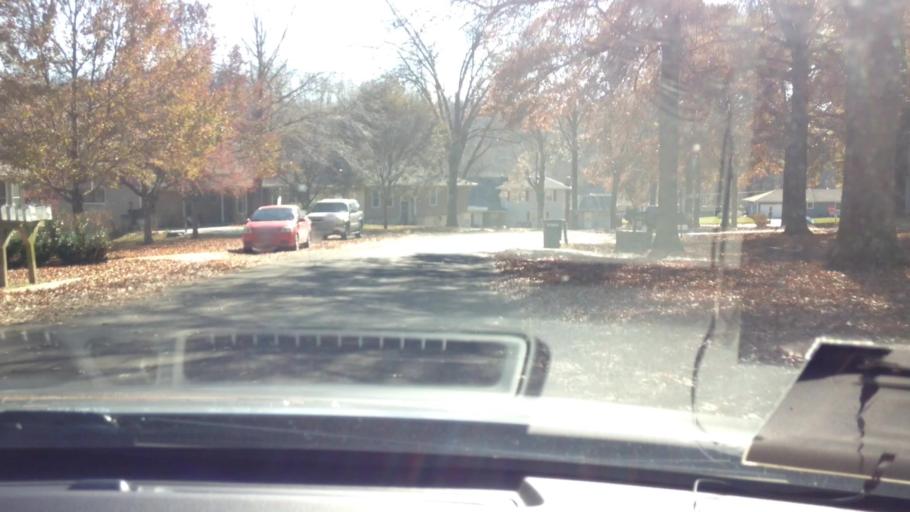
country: US
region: Missouri
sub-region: Platte County
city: Weston
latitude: 39.4117
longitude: -94.8873
